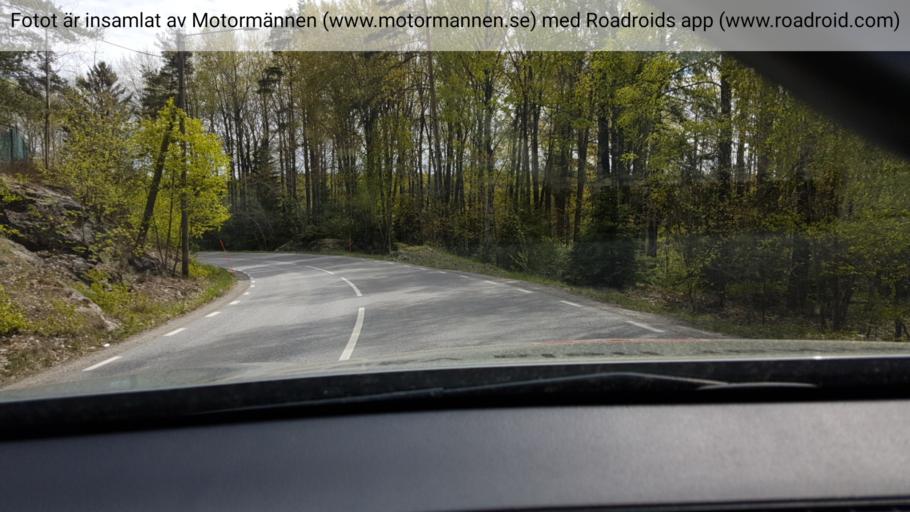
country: SE
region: Stockholm
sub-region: Haninge Kommun
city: Haninge
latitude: 59.1635
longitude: 18.1622
